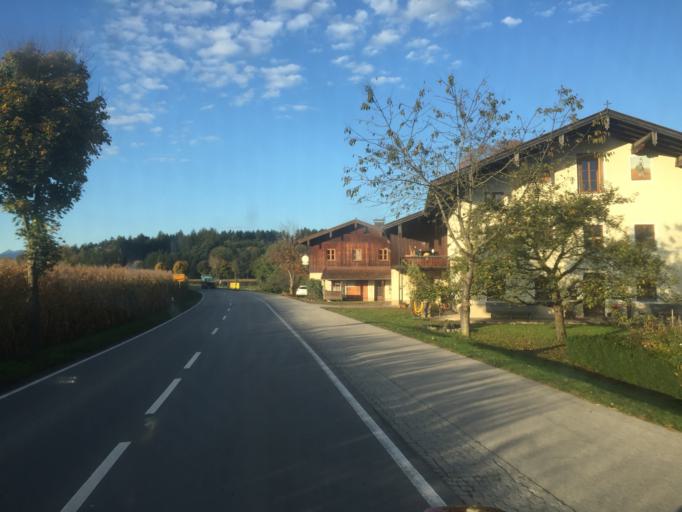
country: DE
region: Bavaria
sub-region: Upper Bavaria
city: Chieming
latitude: 47.9101
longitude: 12.5591
